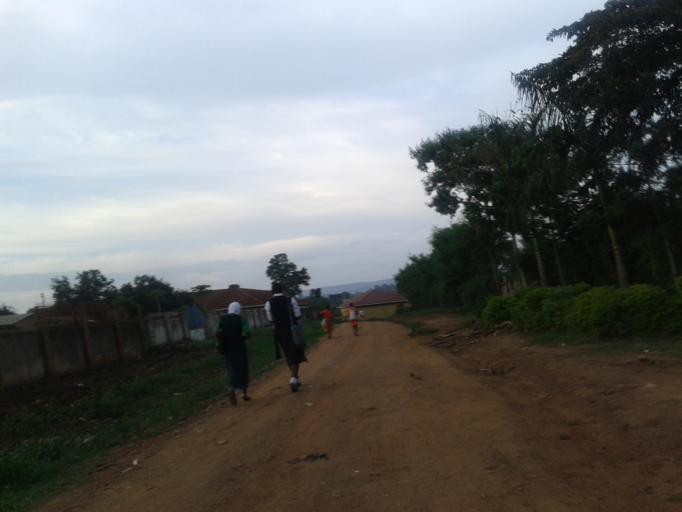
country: UG
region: Eastern Region
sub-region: Mbale District
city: Mbale
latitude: 1.0817
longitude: 34.1771
